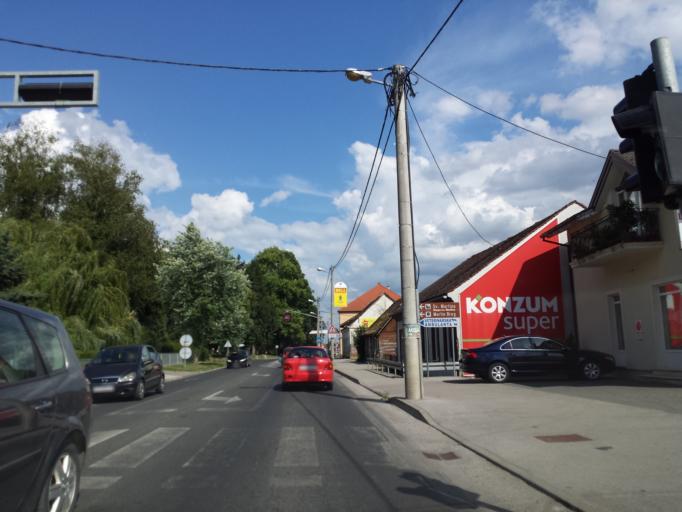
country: HR
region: Zagrebacka
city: Brckovljani
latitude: 45.8065
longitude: 16.2275
